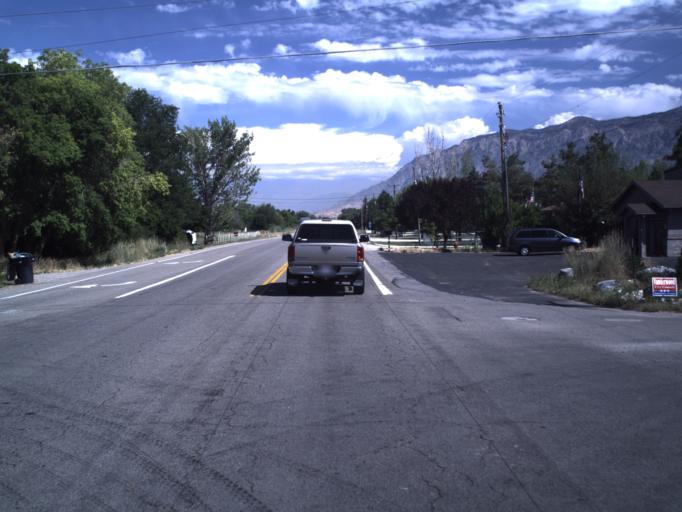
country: US
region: Utah
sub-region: Weber County
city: Marriott-Slaterville
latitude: 41.2517
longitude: -112.0252
